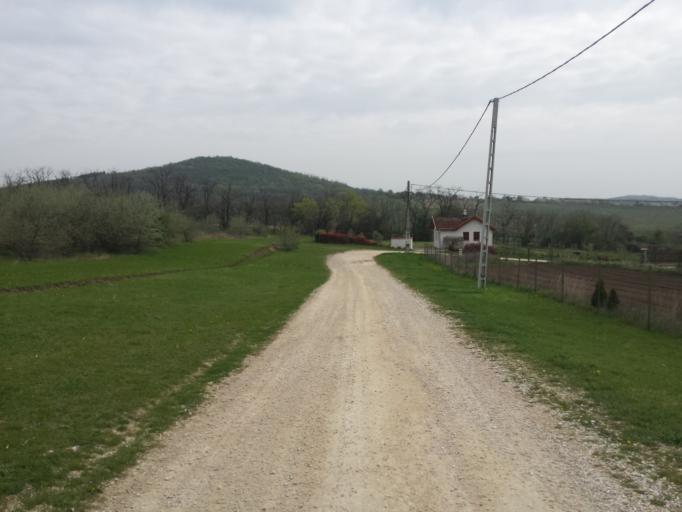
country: HU
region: Fejer
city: Pazmand
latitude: 47.2623
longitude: 18.6193
